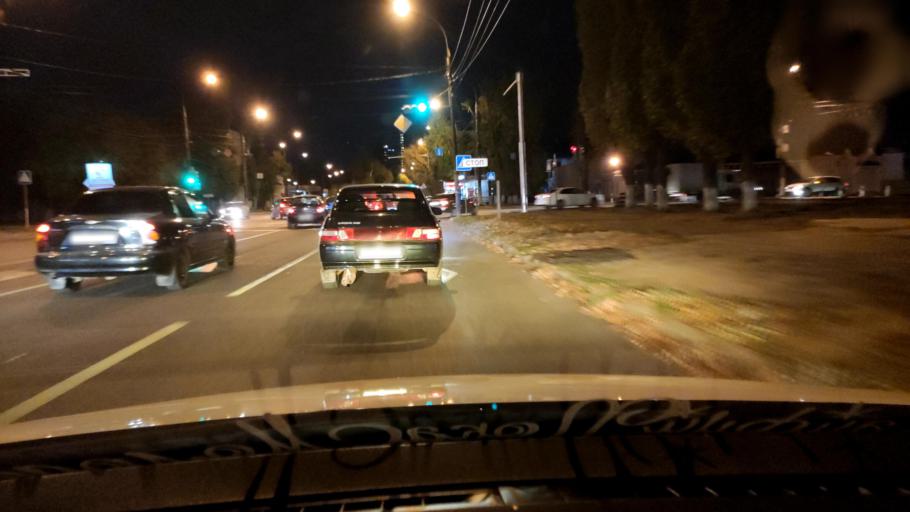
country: RU
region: Voronezj
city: Voronezh
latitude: 51.6822
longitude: 39.1659
